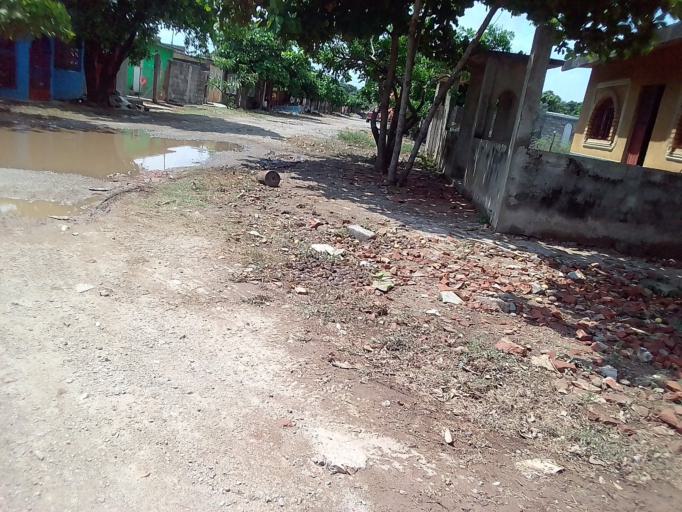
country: MX
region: Oaxaca
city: Union Hidalgo
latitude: 16.4654
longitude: -94.8277
